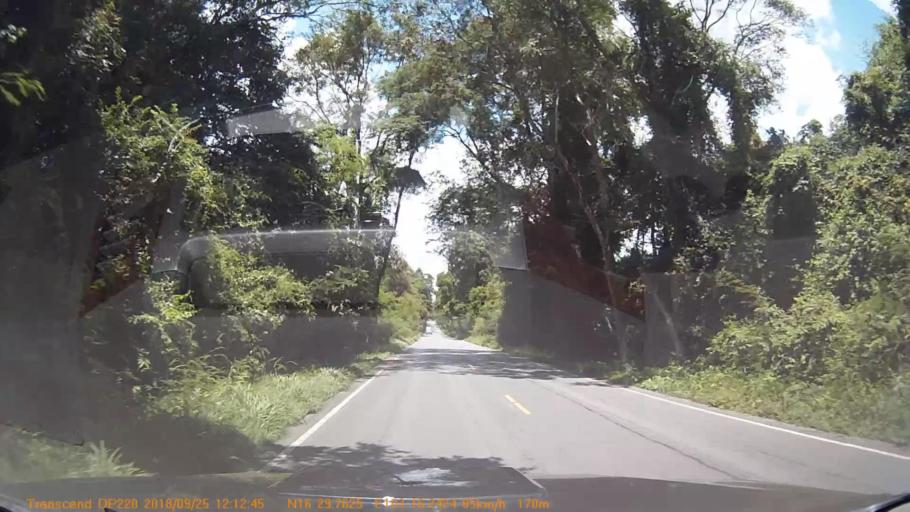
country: TH
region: Kalasin
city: Huai Mek
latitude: 16.4961
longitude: 103.2707
